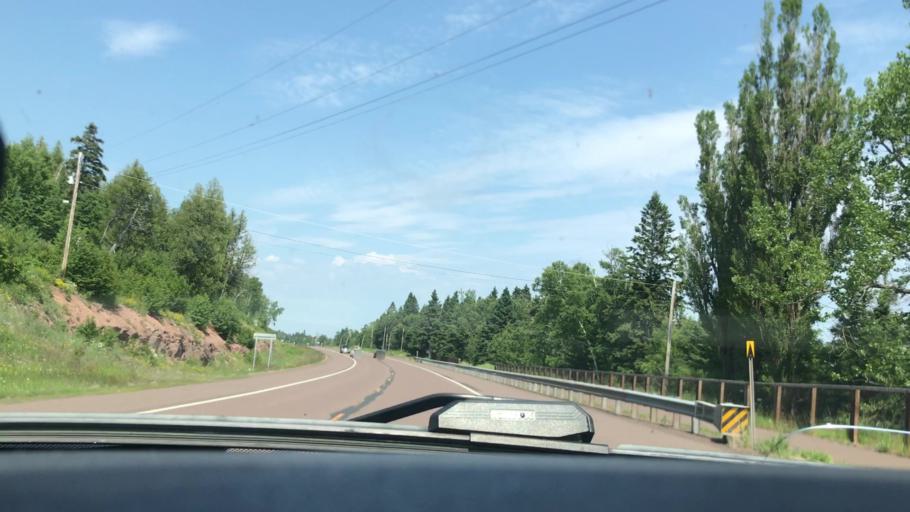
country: US
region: Minnesota
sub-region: Cook County
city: Grand Marais
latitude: 47.6101
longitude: -90.7659
